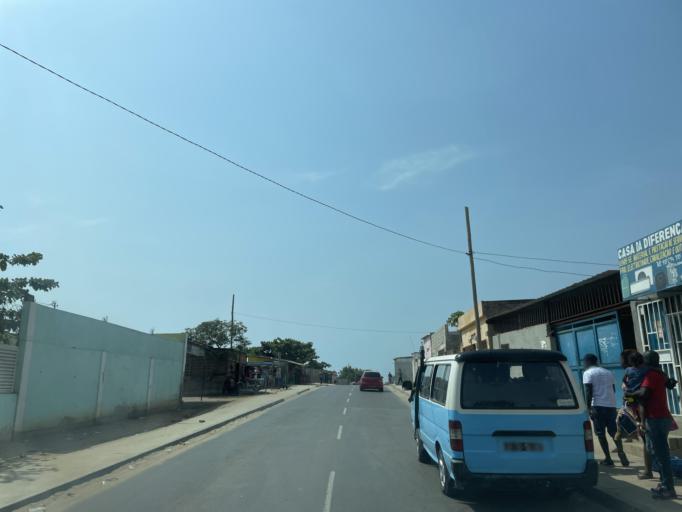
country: AO
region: Luanda
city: Luanda
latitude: -8.9326
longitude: 13.2051
